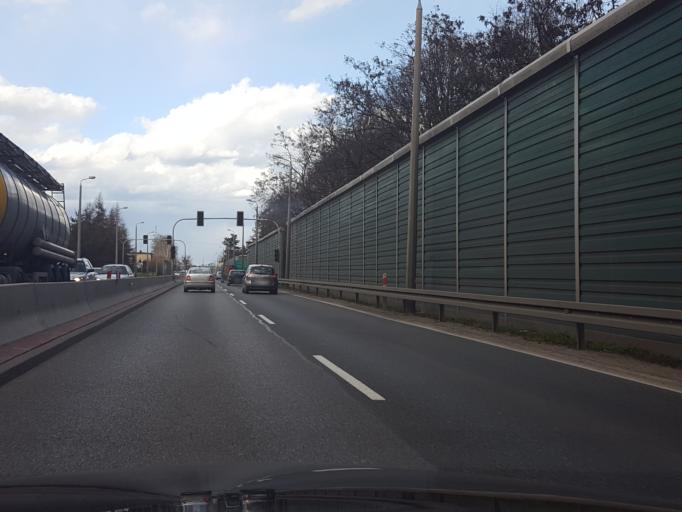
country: PL
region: Silesian Voivodeship
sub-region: Powiat pszczynski
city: Pszczyna
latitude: 49.9692
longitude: 18.9583
